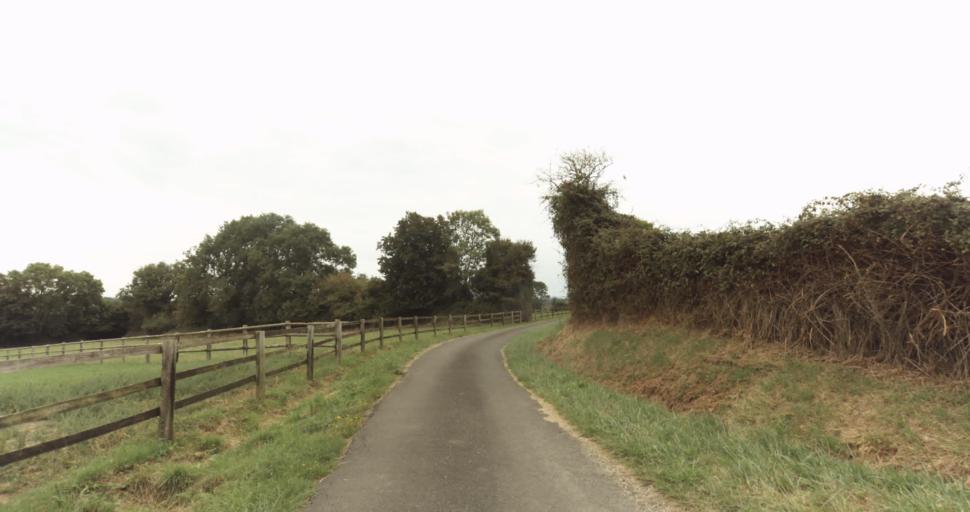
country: FR
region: Lower Normandy
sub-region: Departement de l'Orne
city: Sees
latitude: 48.6773
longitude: 0.2454
